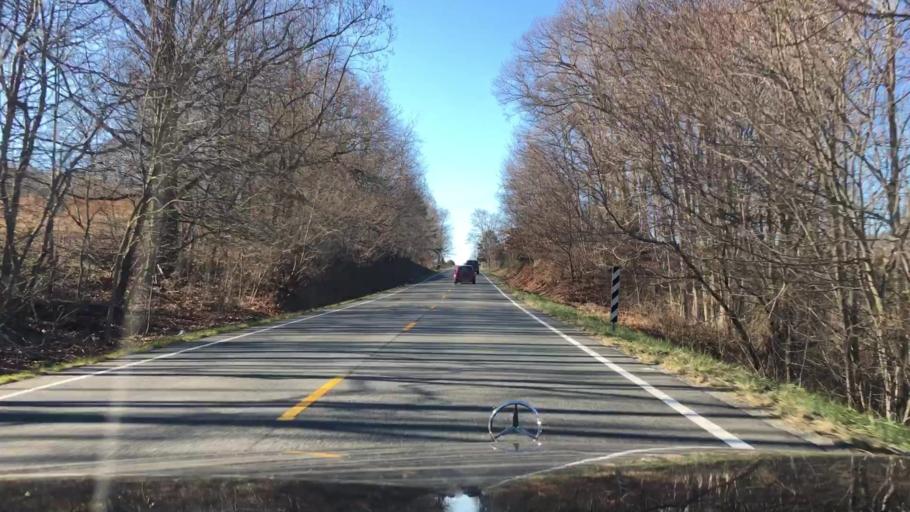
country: US
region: Virginia
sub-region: Franklin County
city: North Shore
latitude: 37.2409
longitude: -79.6645
